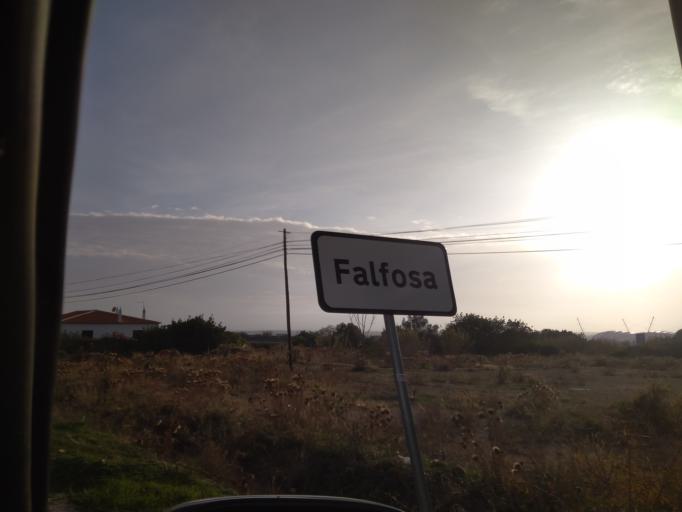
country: PT
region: Faro
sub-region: Faro
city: Santa Barbara de Nexe
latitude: 37.0955
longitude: -7.9633
